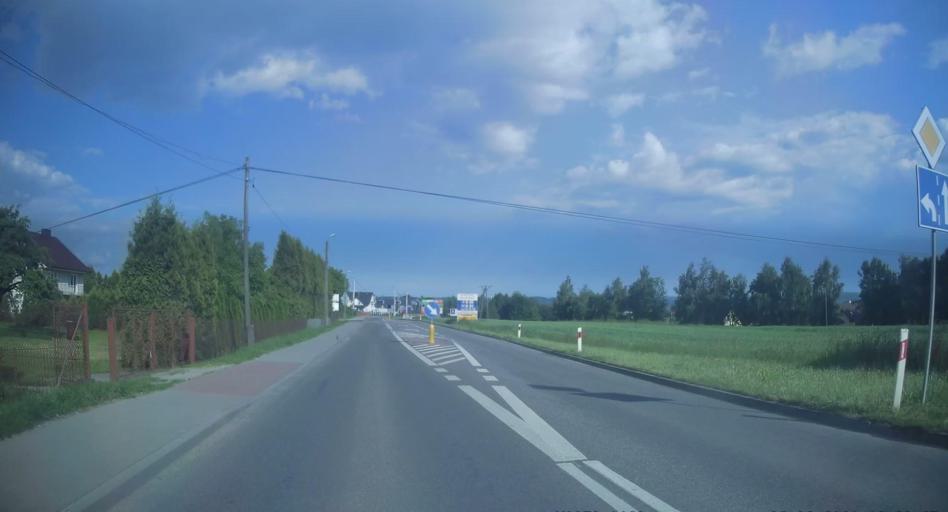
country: PL
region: Subcarpathian Voivodeship
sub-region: Powiat debicki
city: Zyrakow
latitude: 50.0719
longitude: 21.3946
